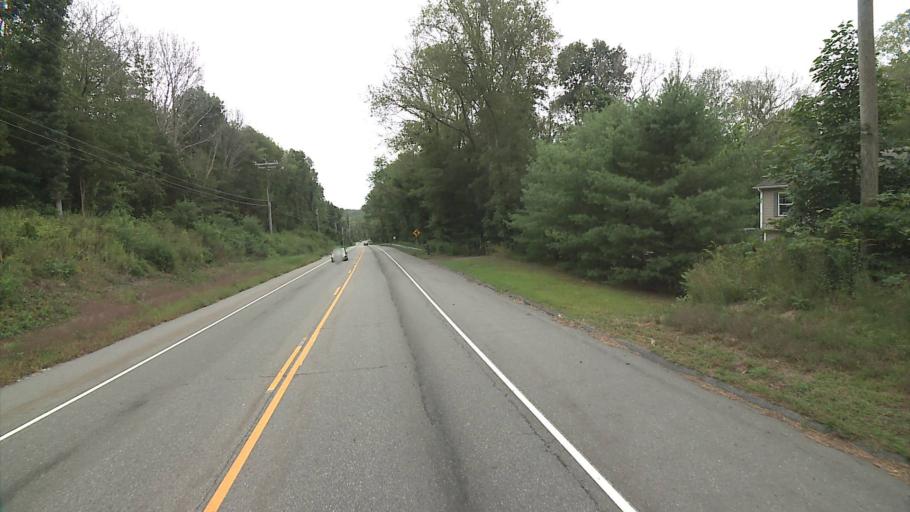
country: US
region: Connecticut
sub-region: New London County
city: Montville Center
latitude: 41.4452
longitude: -72.2315
